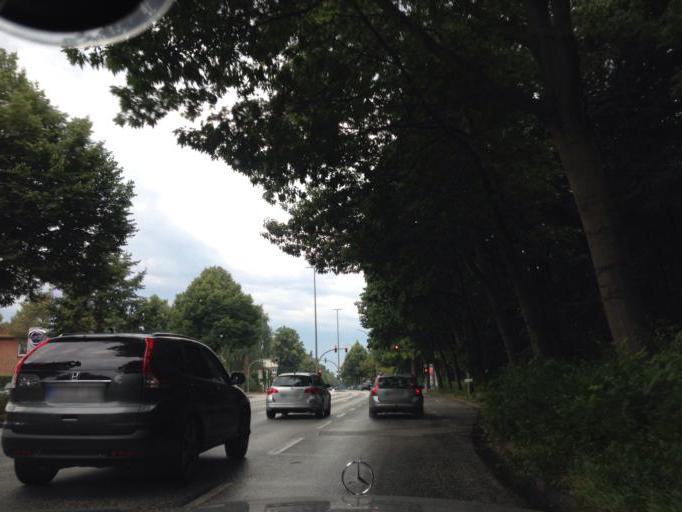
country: DE
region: Hamburg
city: Wellingsbuettel
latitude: 53.6401
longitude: 10.0956
